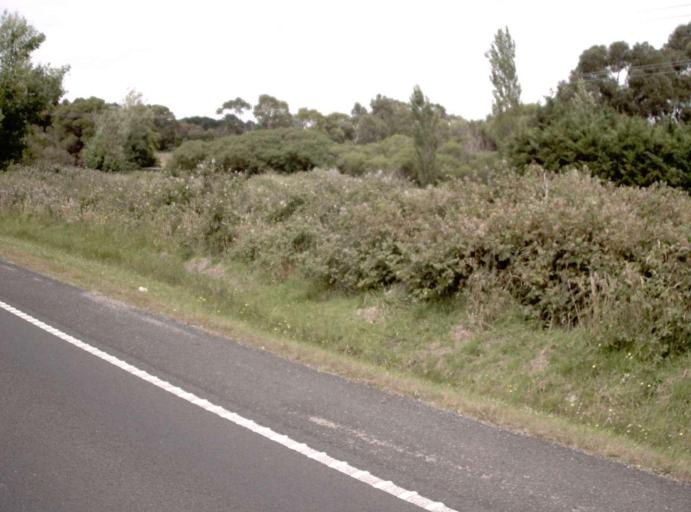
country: AU
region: Victoria
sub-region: Mornington Peninsula
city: Tyabb
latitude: -38.2491
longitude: 145.2150
